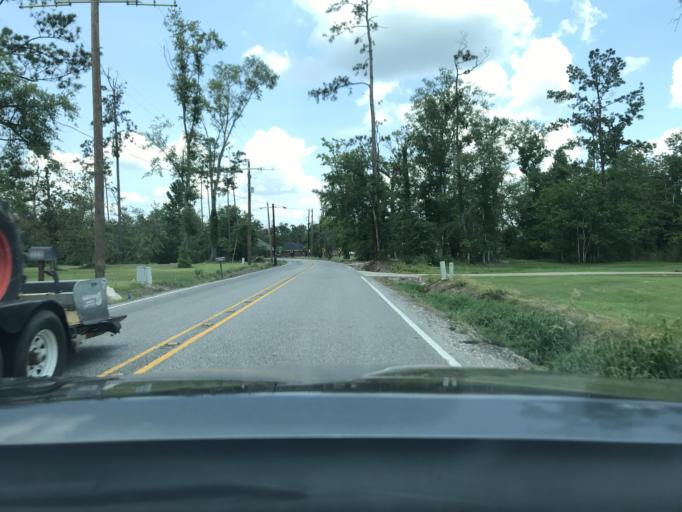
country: US
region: Louisiana
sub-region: Calcasieu Parish
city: Moss Bluff
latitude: 30.3257
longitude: -93.1726
